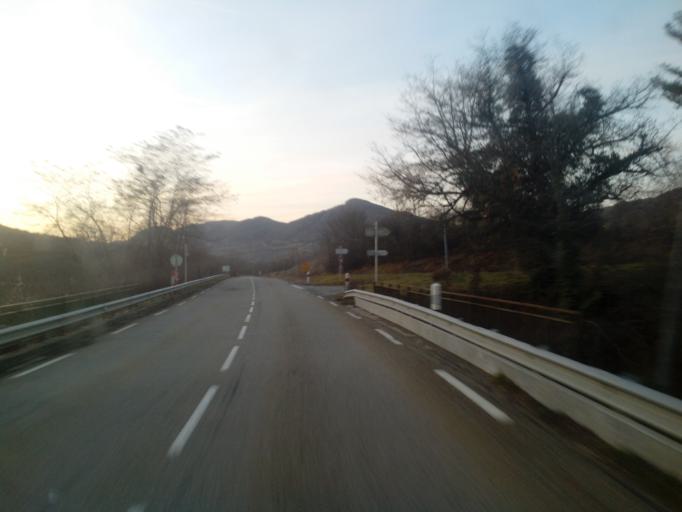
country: FR
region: Midi-Pyrenees
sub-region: Departement de l'Ariege
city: Saint-Paul-de-Jarrat
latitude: 42.9241
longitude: 1.7501
